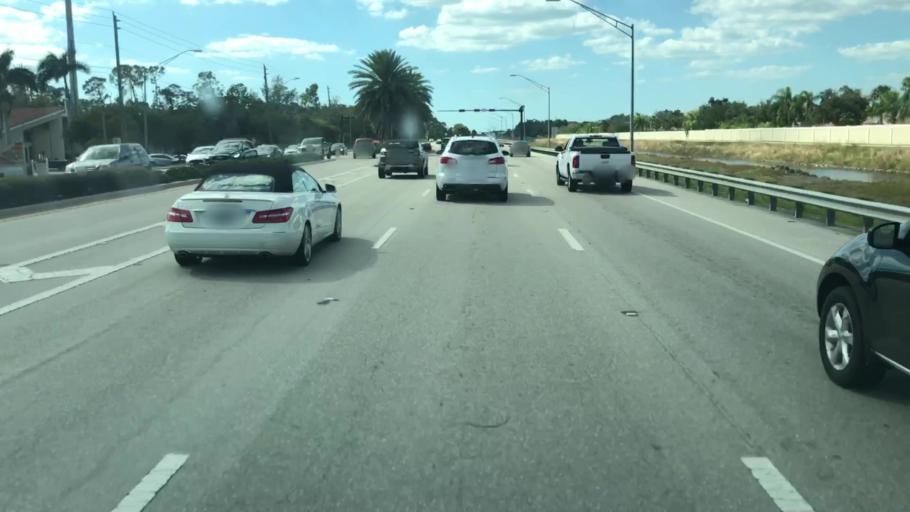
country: US
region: Florida
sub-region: Collier County
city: Vineyards
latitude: 26.2730
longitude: -81.7238
